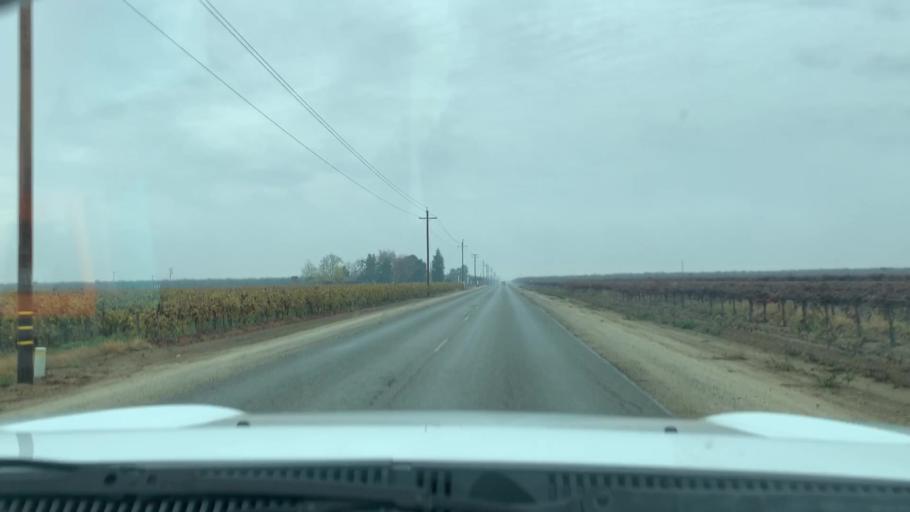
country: US
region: California
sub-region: Kern County
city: Delano
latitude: 35.7611
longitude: -119.3696
